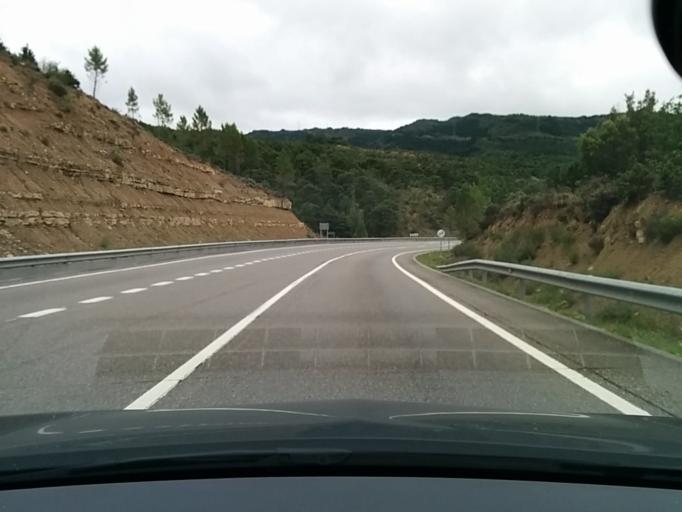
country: ES
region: Aragon
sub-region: Provincia de Huesca
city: Arguis
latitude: 42.3987
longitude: -0.3830
